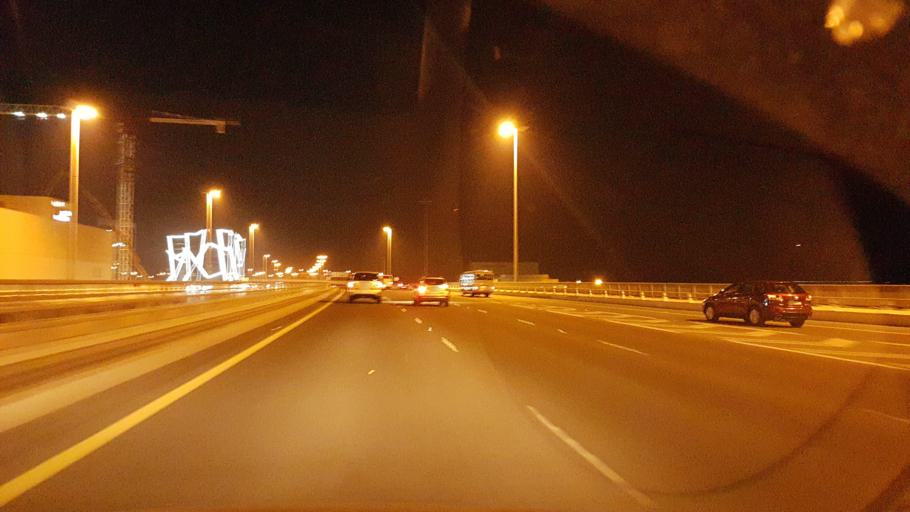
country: BH
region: Muharraq
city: Al Muharraq
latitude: 26.2485
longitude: 50.5877
